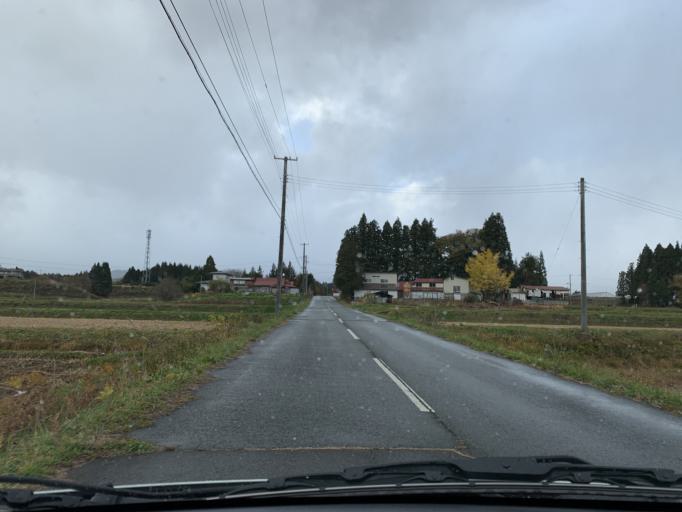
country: JP
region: Iwate
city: Mizusawa
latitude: 39.0941
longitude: 140.9899
